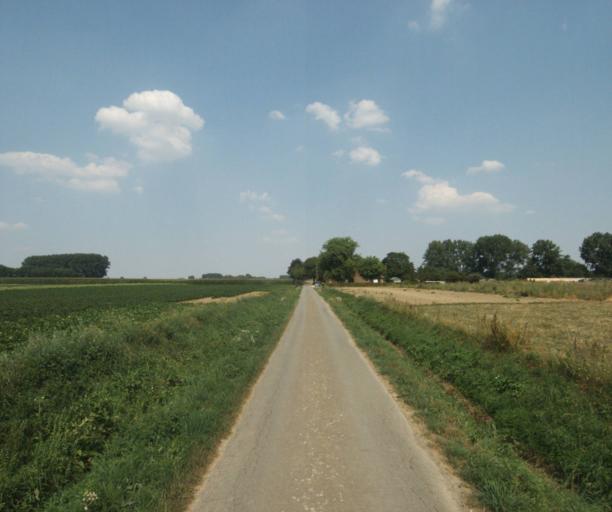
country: FR
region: Nord-Pas-de-Calais
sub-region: Departement du Nord
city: Quesnoy-sur-Deule
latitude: 50.7237
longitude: 3.0002
